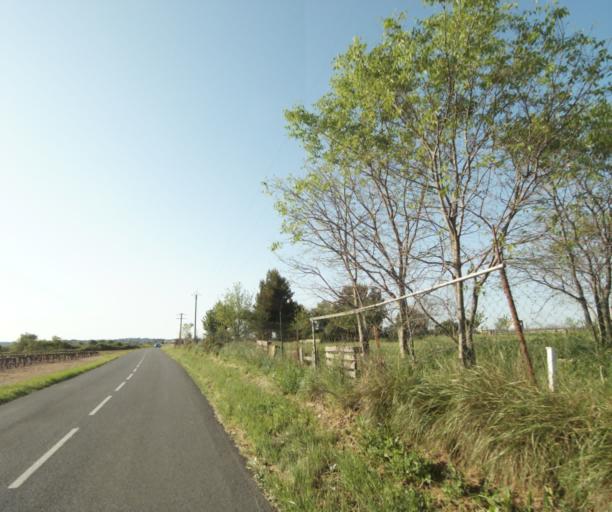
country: FR
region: Languedoc-Roussillon
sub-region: Departement de l'Herault
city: Laverune
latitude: 43.5950
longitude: 3.7956
